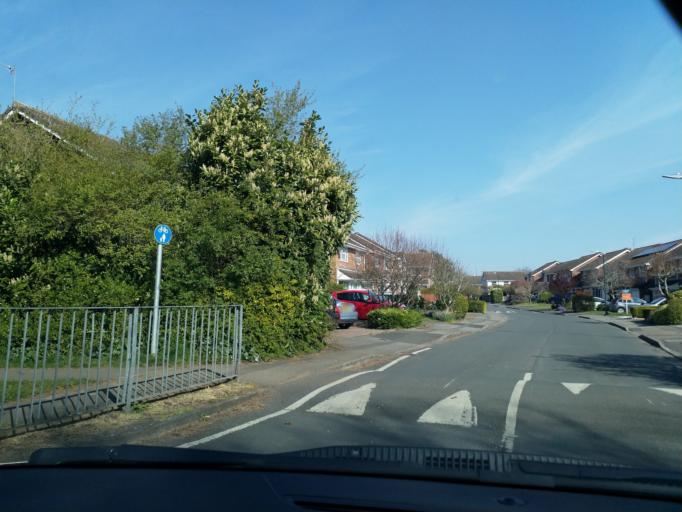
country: GB
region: England
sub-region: Warwickshire
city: Stratford-upon-Avon
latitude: 52.1843
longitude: -1.7245
